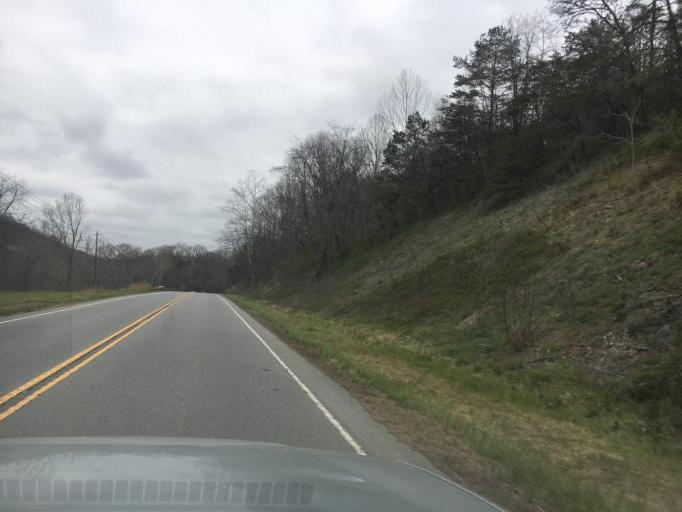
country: US
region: North Carolina
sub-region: Madison County
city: Mars Hill
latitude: 35.7839
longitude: -82.4665
